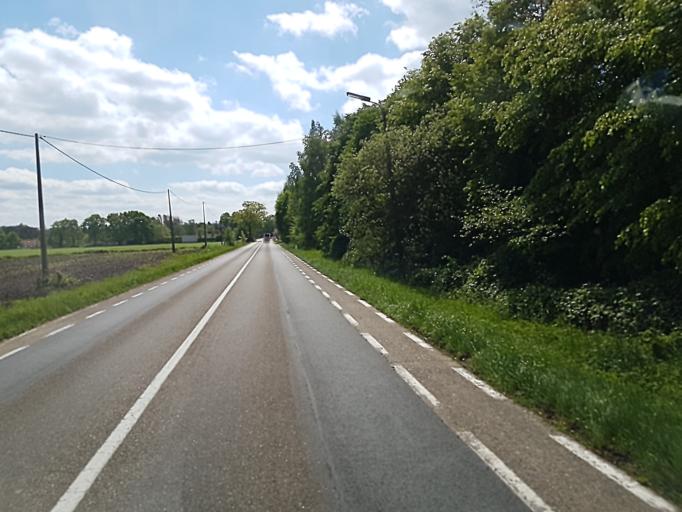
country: BE
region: Flanders
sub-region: Provincie Antwerpen
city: Laakdal
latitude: 51.0621
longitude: 4.9931
